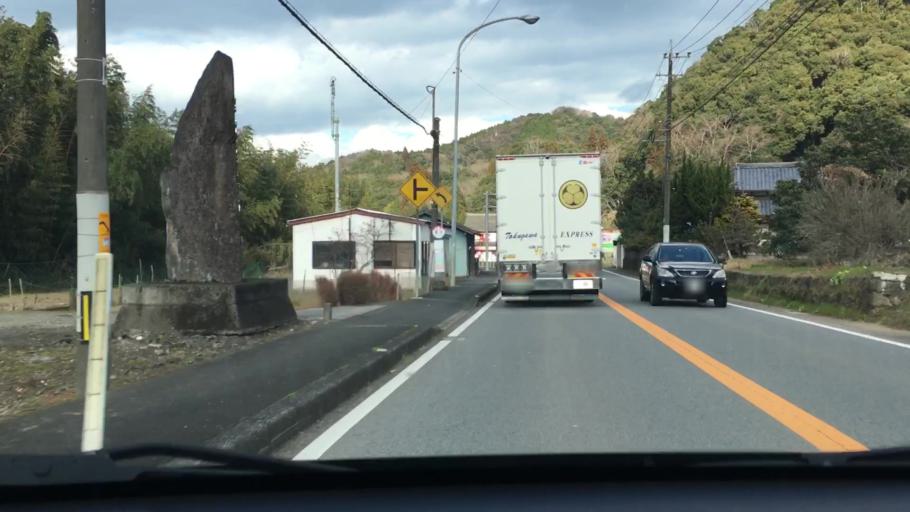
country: JP
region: Oita
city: Usuki
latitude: 33.0162
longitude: 131.7008
